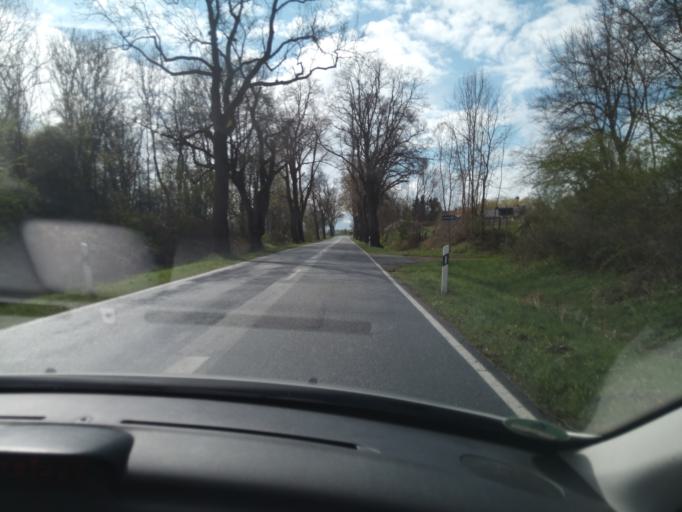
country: DE
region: Mecklenburg-Vorpommern
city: Loitz
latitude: 53.4611
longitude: 13.3601
